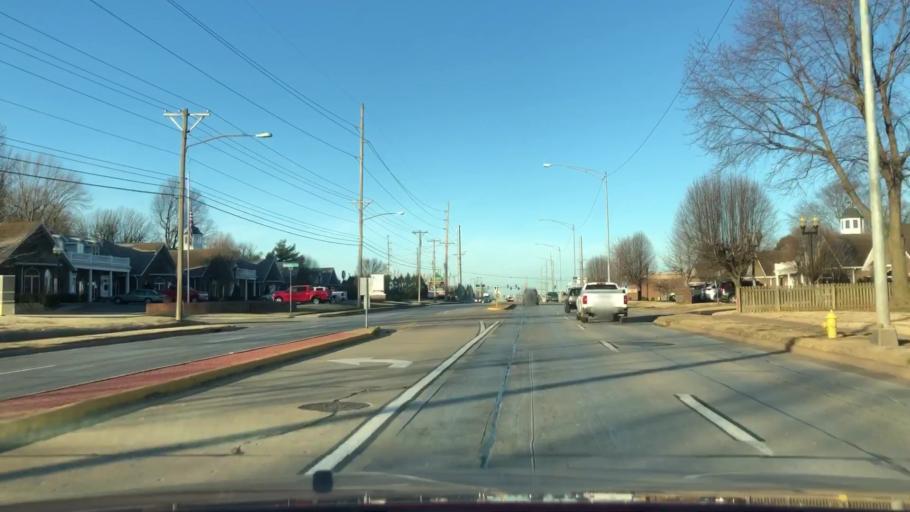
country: US
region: Missouri
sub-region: Greene County
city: Springfield
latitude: 37.1593
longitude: -93.2588
